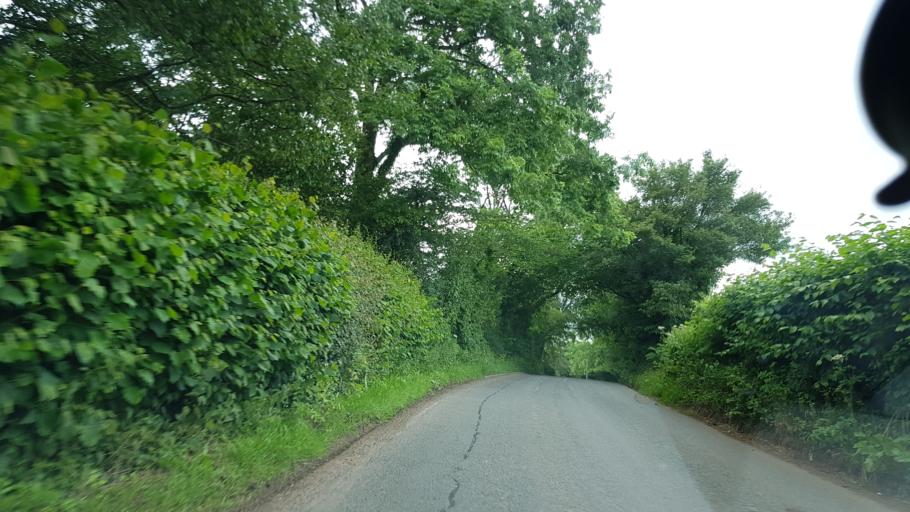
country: GB
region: England
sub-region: Herefordshire
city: Llancillo
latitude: 51.8958
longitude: -2.9353
